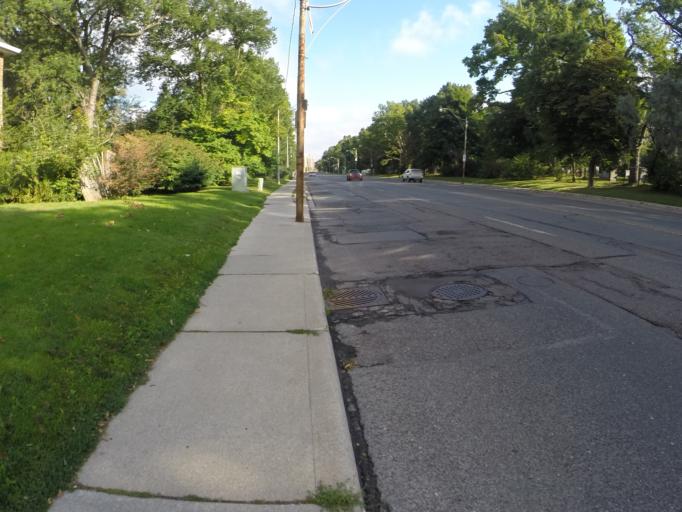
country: CA
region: Ontario
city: Toronto
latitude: 43.6937
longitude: -79.3848
